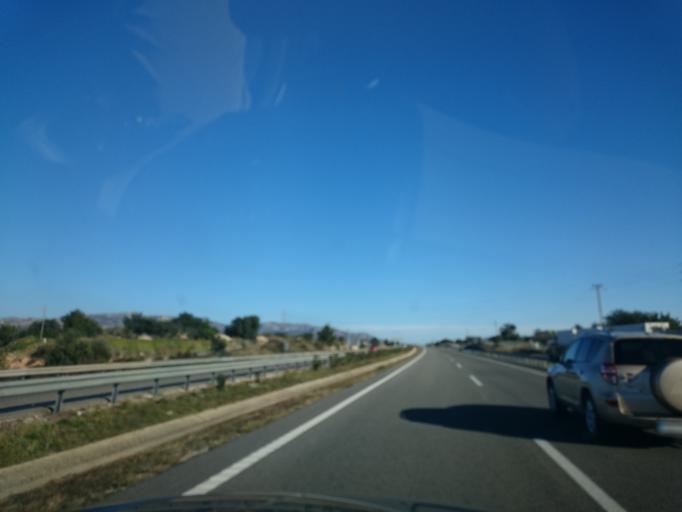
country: ES
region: Catalonia
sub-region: Provincia de Tarragona
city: l'Ametlla de Mar
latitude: 40.8890
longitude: 0.8017
